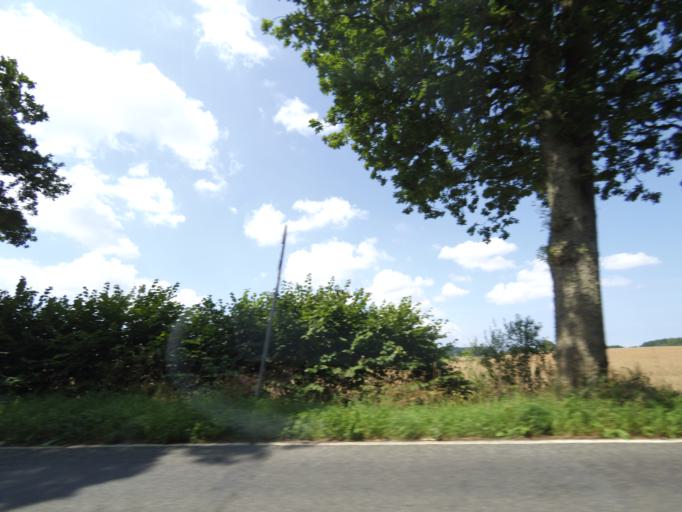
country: DK
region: South Denmark
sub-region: Assens Kommune
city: Arup
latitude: 55.3960
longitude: 10.0439
